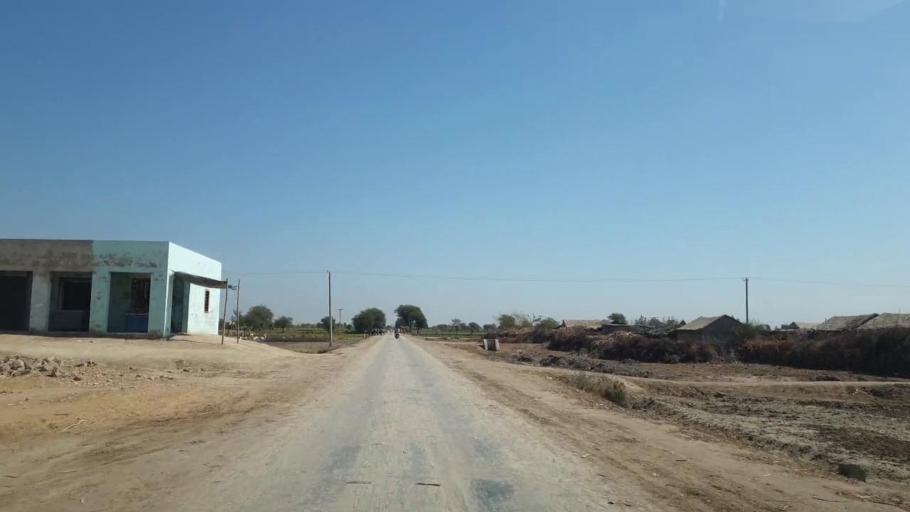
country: PK
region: Sindh
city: Mirpur Khas
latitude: 25.5962
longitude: 69.0838
